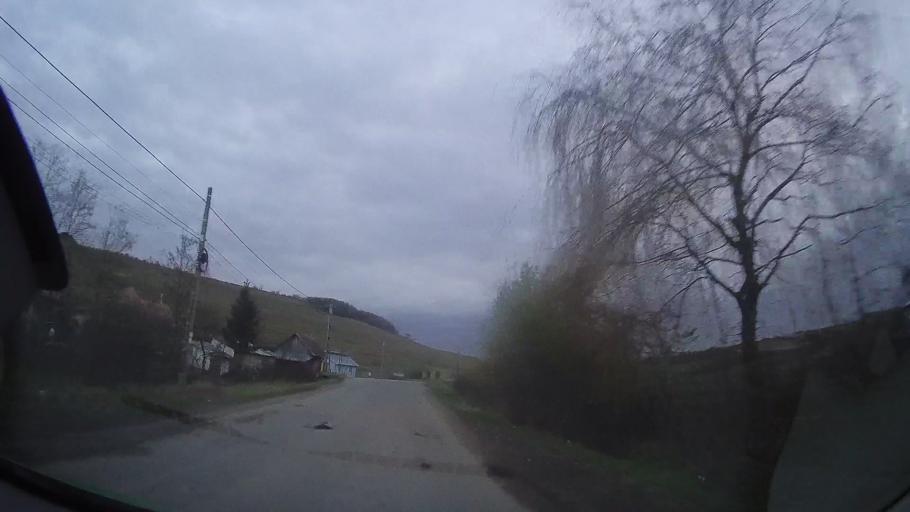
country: RO
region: Cluj
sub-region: Comuna Caianu
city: Vaida-Camaras
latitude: 46.8219
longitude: 23.9383
